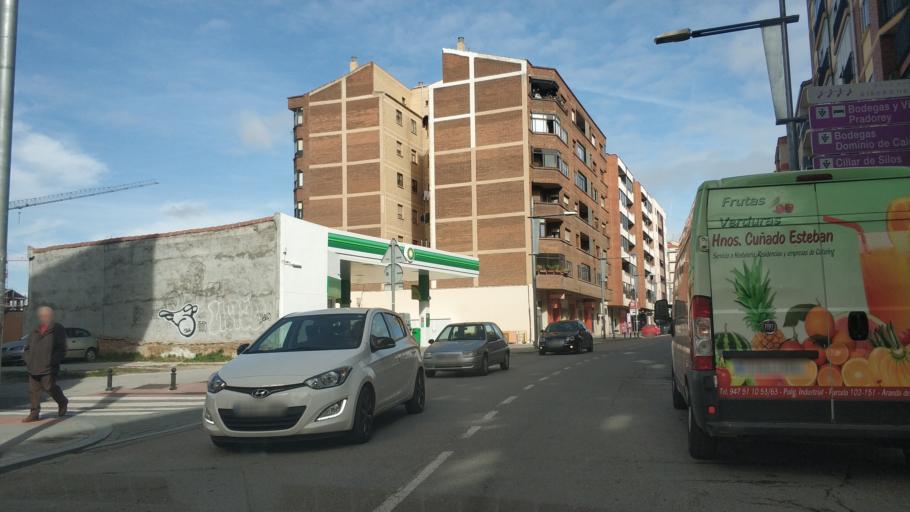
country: ES
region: Castille and Leon
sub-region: Provincia de Burgos
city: Aranda de Duero
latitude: 41.6746
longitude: -3.6859
